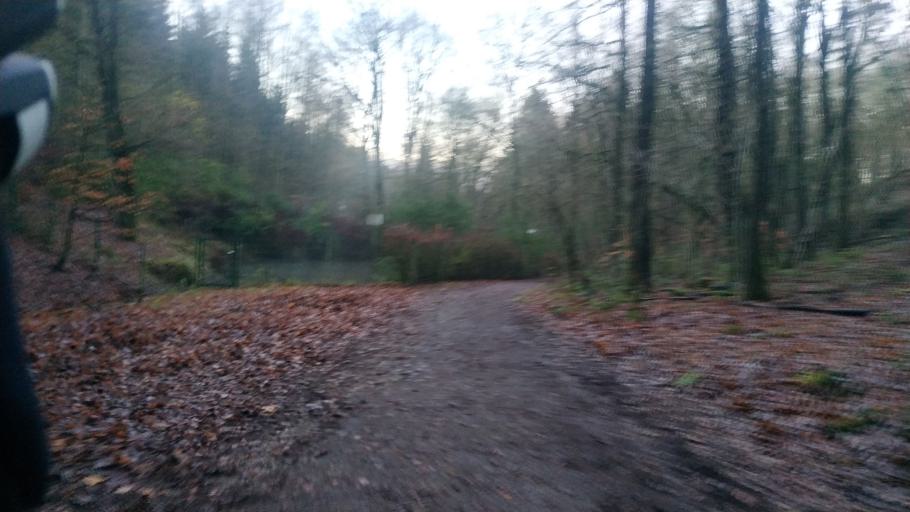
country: DE
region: North Rhine-Westphalia
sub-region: Regierungsbezirk Munster
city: Mettingen
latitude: 52.3023
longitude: 7.7734
